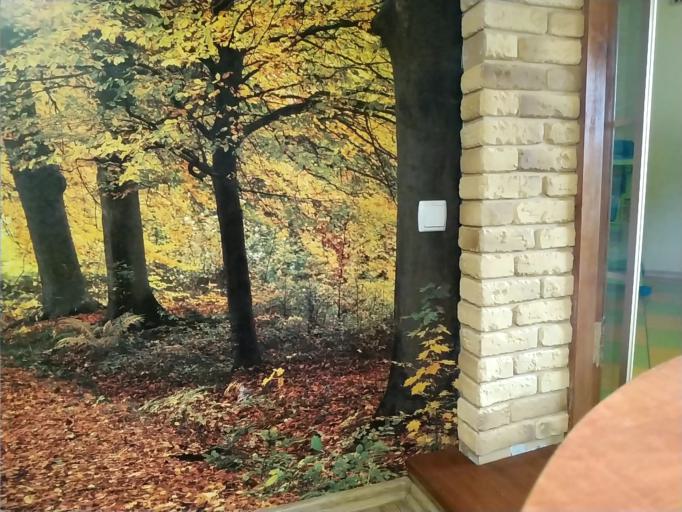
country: RU
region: Smolensk
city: Dorogobuzh
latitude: 54.8850
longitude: 33.3107
